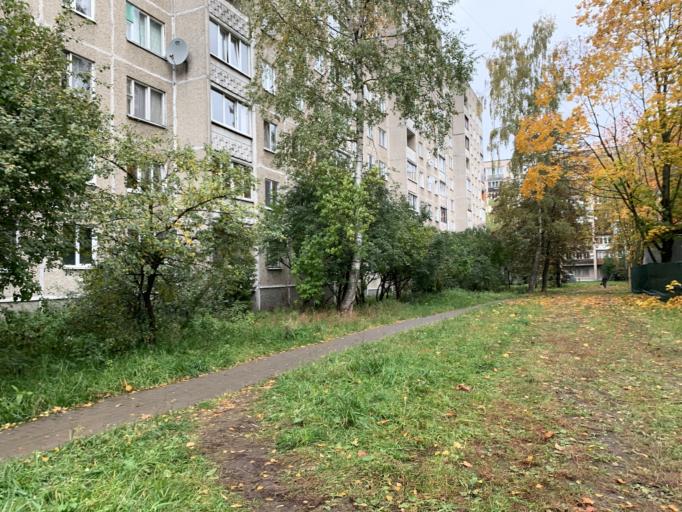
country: BY
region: Minsk
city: Minsk
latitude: 53.9369
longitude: 27.6007
